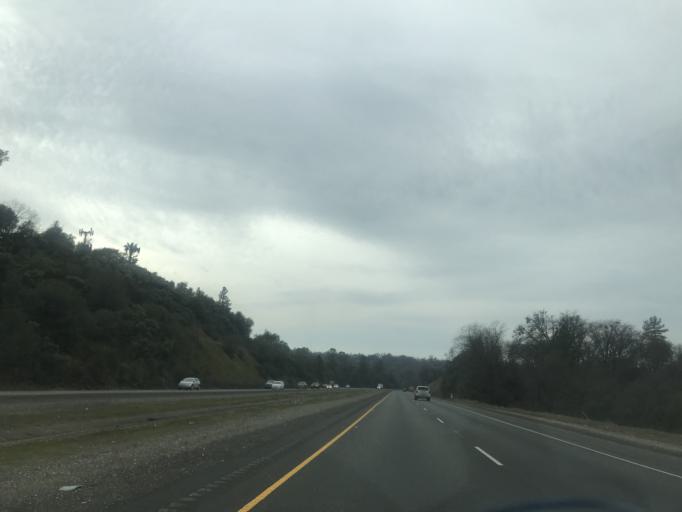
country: US
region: California
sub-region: El Dorado County
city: Deer Park
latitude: 38.6982
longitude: -120.8757
